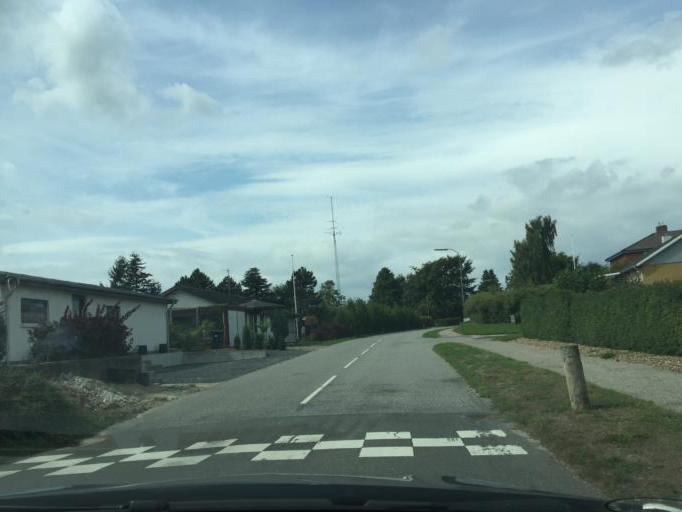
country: DK
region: South Denmark
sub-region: Assens Kommune
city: Tommerup Stationsby
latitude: 55.3896
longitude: 10.1911
